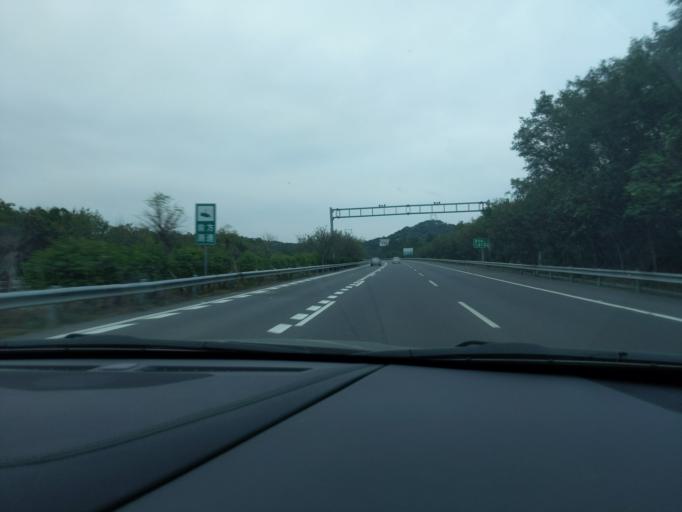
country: CN
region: Fujian
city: Shishi
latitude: 24.7500
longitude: 118.5929
